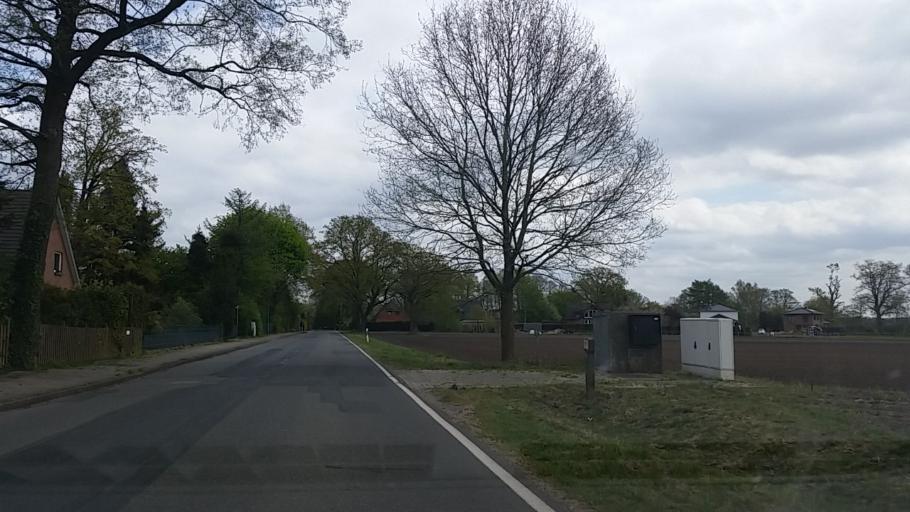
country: DE
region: Lower Saxony
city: Otter
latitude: 53.2344
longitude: 9.7371
